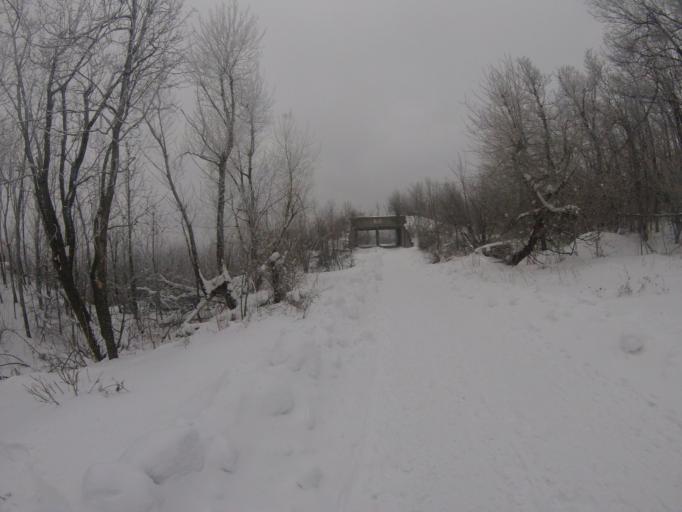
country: HU
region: Pest
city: Pilisszanto
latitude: 47.6891
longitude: 18.8696
